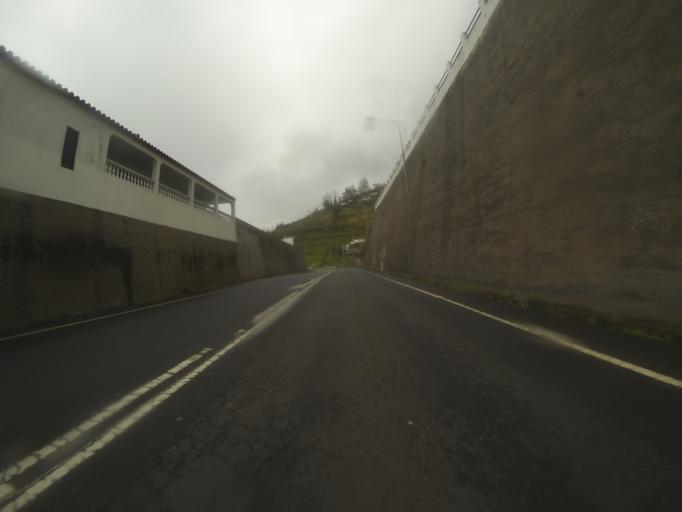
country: PT
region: Madeira
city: Canico
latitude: 32.6478
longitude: -16.8661
